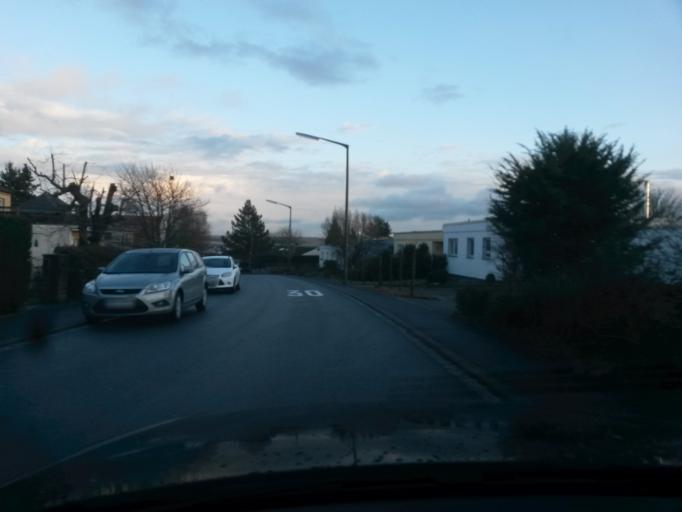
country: DE
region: Bavaria
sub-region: Regierungsbezirk Unterfranken
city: Estenfeld
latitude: 49.8320
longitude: 9.9987
